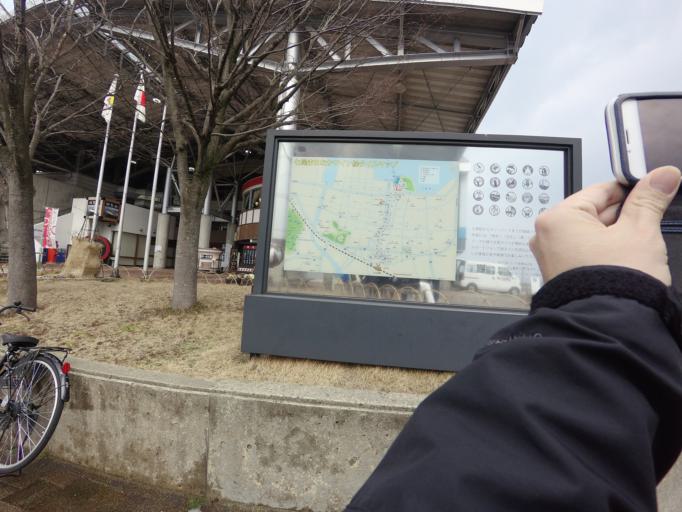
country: JP
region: Ishikawa
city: Nanao
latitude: 37.0482
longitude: 136.9679
